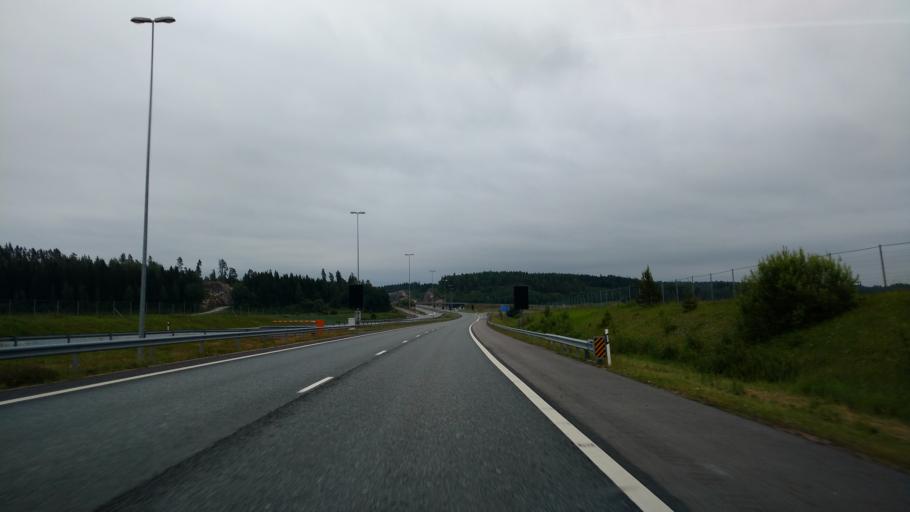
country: FI
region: Varsinais-Suomi
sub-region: Salo
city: Muurla
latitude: 60.3844
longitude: 23.3083
